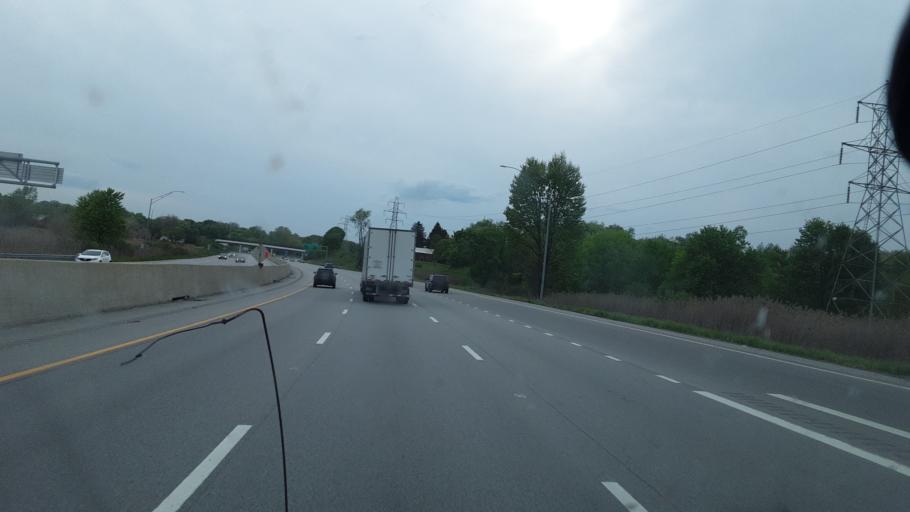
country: US
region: Ohio
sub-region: Summit County
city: Norton
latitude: 41.0414
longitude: -81.6121
